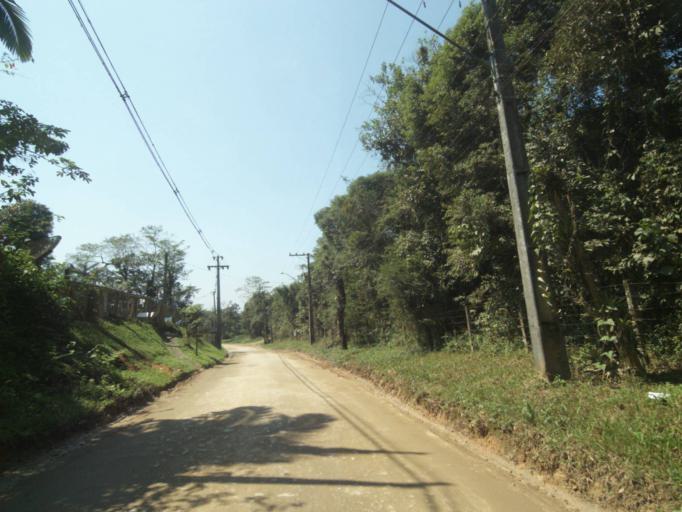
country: BR
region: Parana
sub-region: Paranagua
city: Paranagua
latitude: -25.5644
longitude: -48.6134
